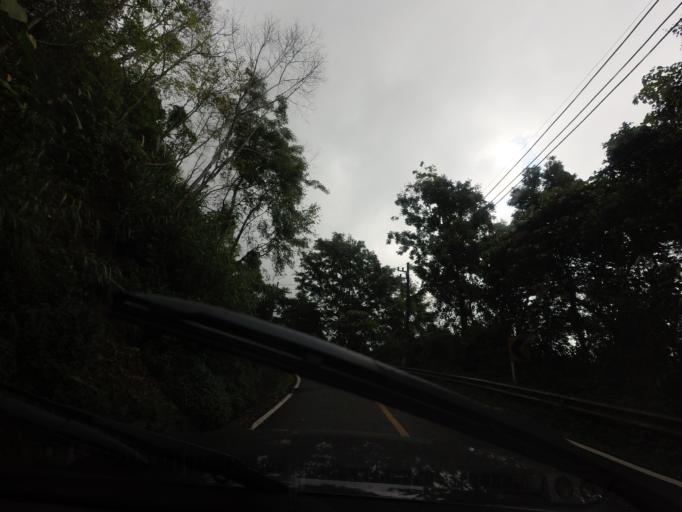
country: TH
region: Nan
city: Bo Kluea
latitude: 19.1792
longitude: 101.0822
